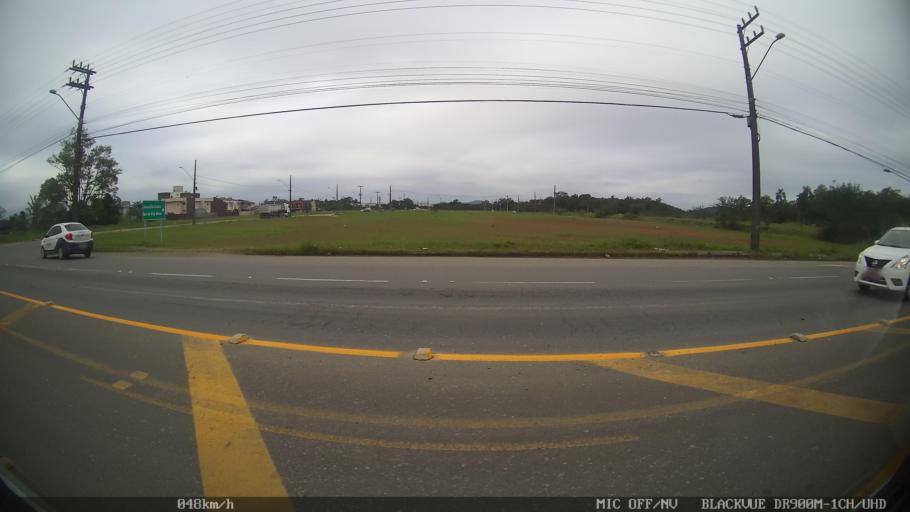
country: BR
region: Santa Catarina
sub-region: Joinville
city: Joinville
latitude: -26.2927
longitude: -48.9203
